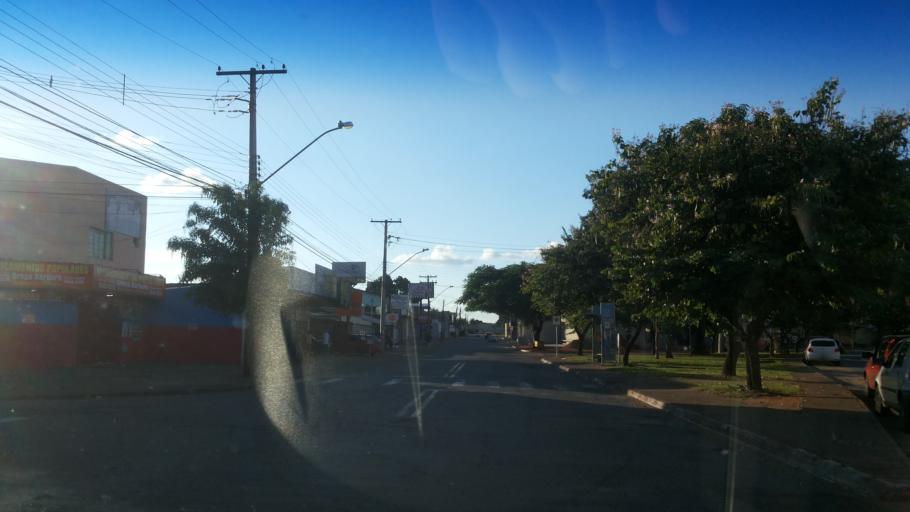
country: BR
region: Goias
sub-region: Goiania
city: Goiania
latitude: -16.7152
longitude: -49.3072
